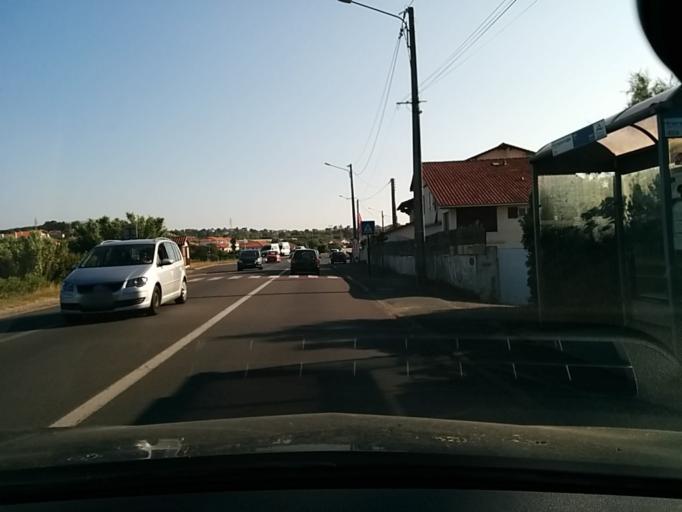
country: FR
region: Aquitaine
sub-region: Departement des Pyrenees-Atlantiques
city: Bidart
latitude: 43.4330
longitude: -1.5959
